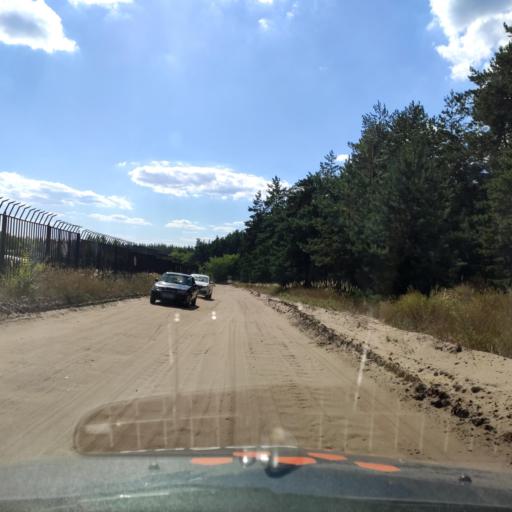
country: RU
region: Voronezj
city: Somovo
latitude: 51.7157
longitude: 39.3734
